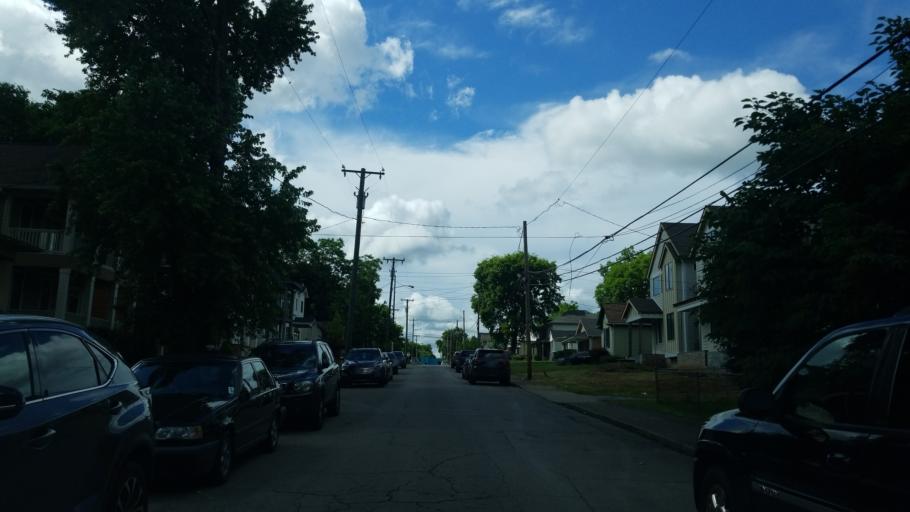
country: US
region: Tennessee
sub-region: Davidson County
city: Nashville
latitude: 36.1686
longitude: -86.7948
